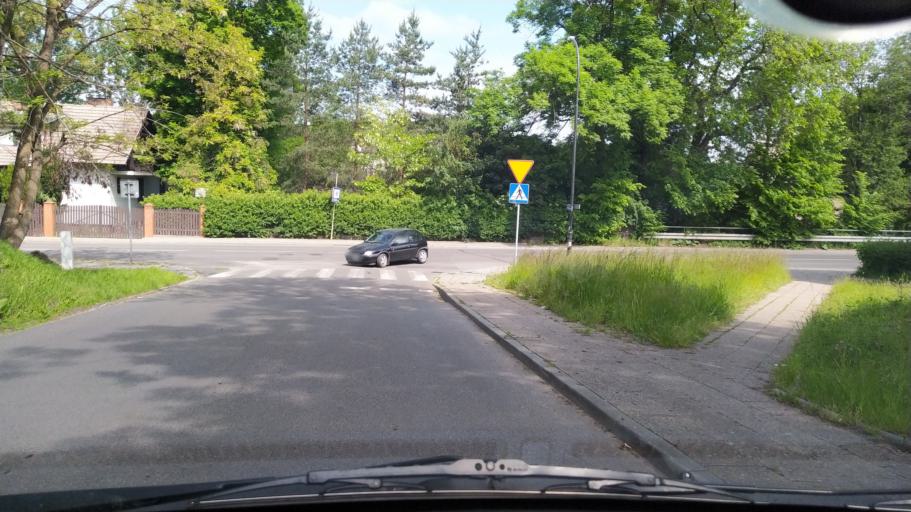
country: PL
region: Silesian Voivodeship
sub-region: Powiat gliwicki
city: Przyszowice
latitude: 50.2892
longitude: 18.7283
